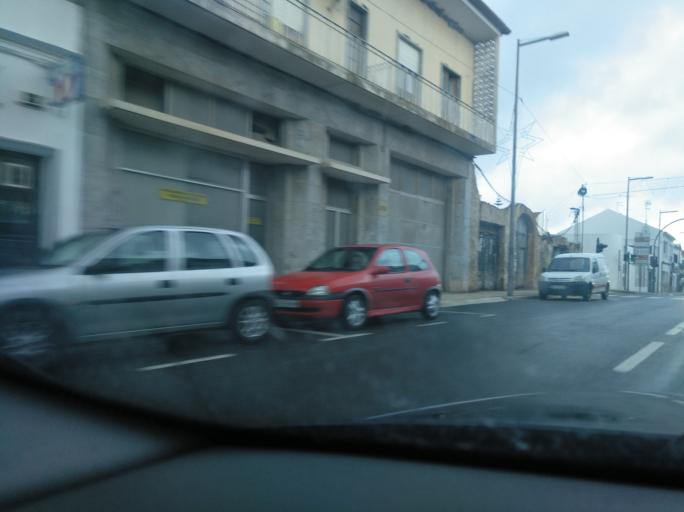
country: PT
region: Beja
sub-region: Aljustrel
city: Aljustrel
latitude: 37.8789
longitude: -8.1638
